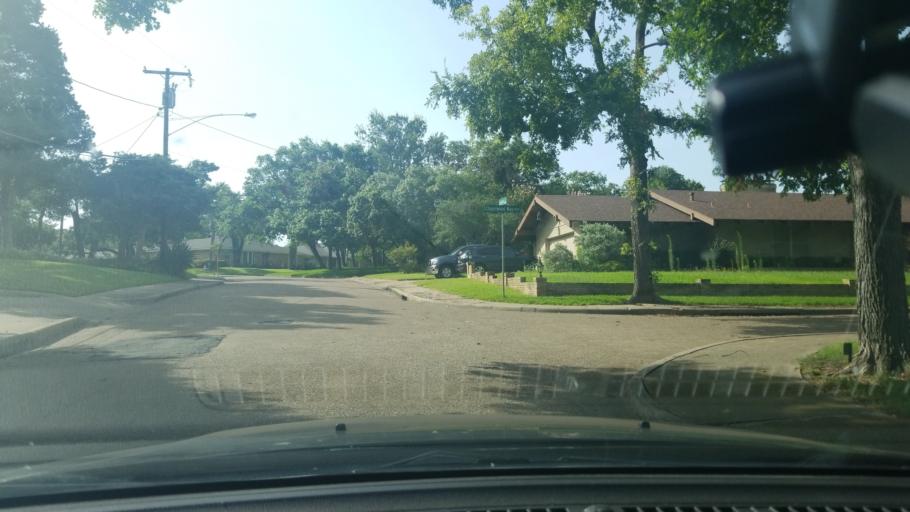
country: US
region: Texas
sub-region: Dallas County
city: Highland Park
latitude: 32.7988
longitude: -96.7016
